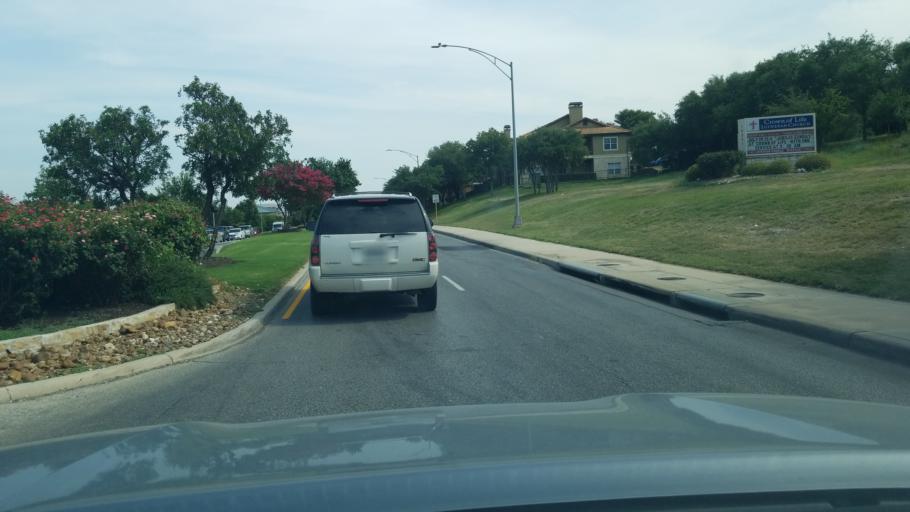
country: US
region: Texas
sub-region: Bexar County
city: Hollywood Park
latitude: 29.6326
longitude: -98.4956
